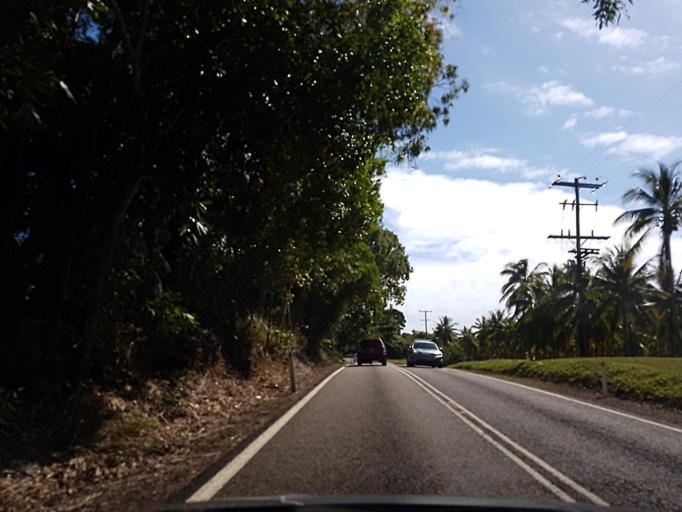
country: AU
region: Queensland
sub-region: Cairns
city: Port Douglas
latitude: -16.5950
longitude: 145.5163
